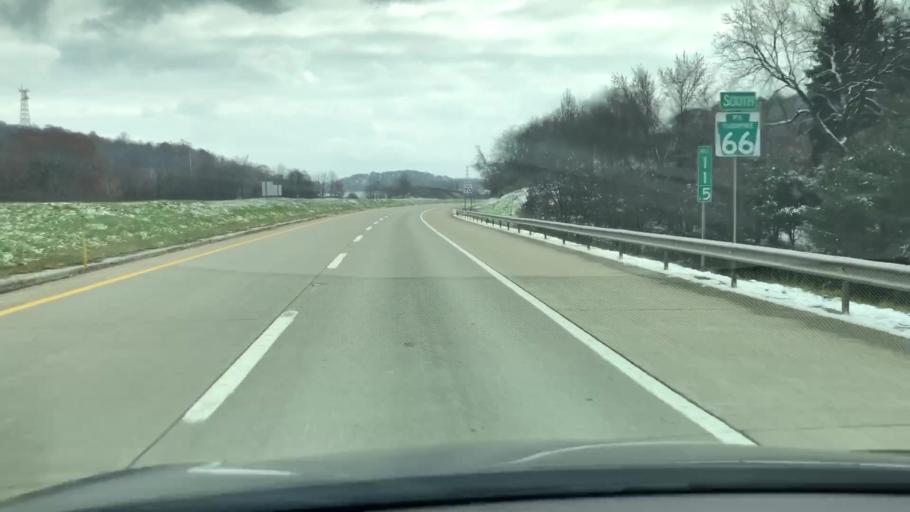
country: US
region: Pennsylvania
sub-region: Westmoreland County
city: Delmont
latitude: 40.3731
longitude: -79.5597
